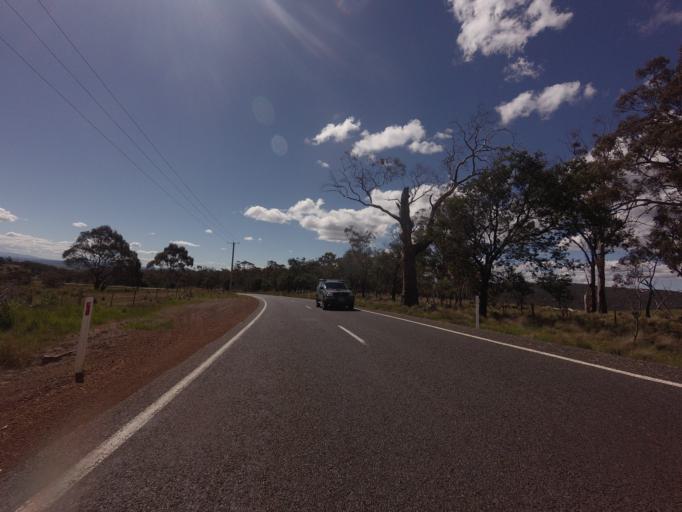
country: AU
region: Tasmania
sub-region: Northern Midlands
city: Evandale
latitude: -41.9428
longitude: 147.6039
